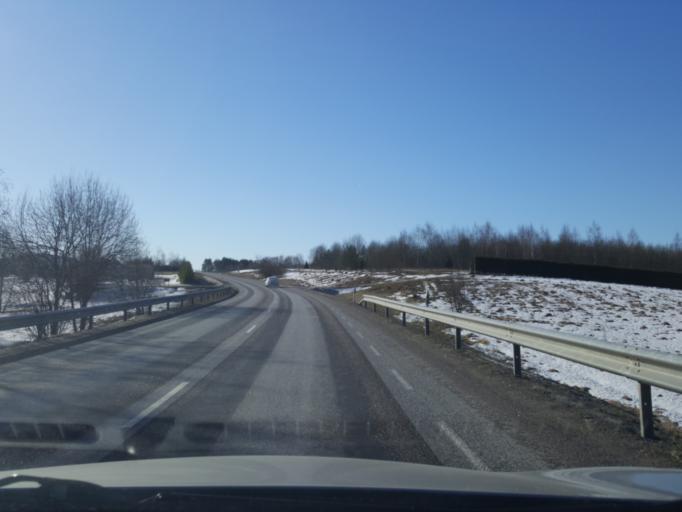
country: EE
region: Viljandimaa
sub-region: Viljandi linn
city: Viljandi
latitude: 58.3843
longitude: 25.6067
